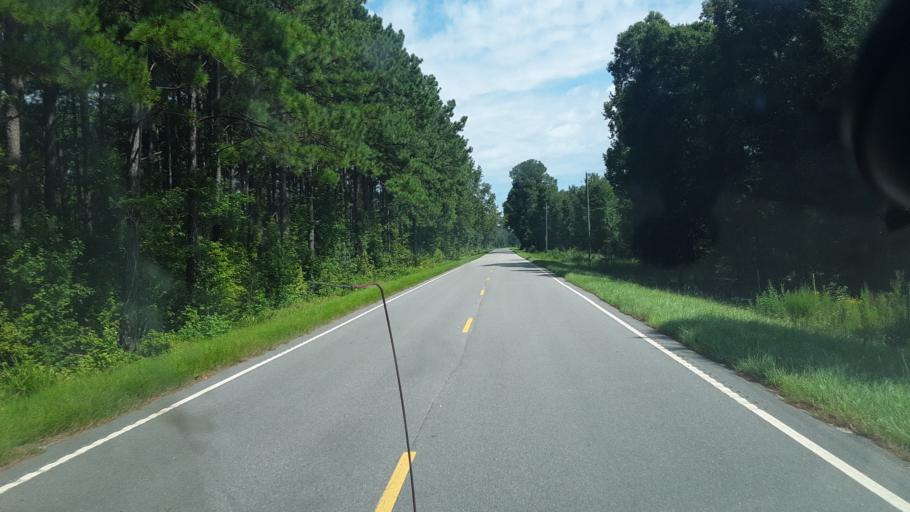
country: US
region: South Carolina
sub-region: Hampton County
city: Hampton
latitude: 33.0677
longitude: -81.0288
